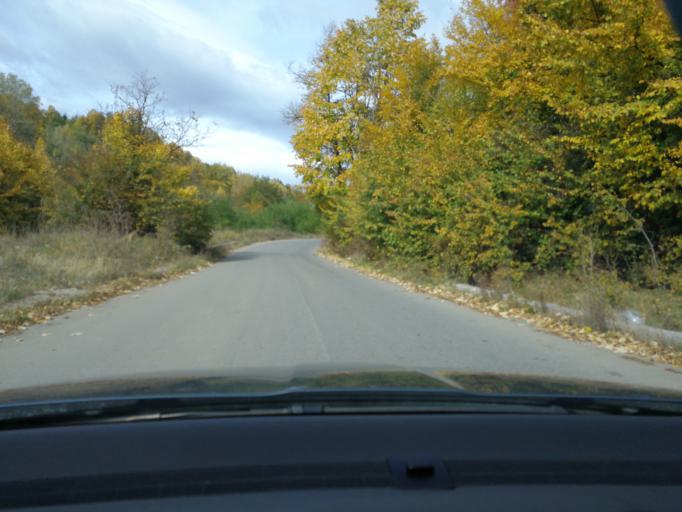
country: RO
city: Brebu Manastirei
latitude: 45.2032
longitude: 25.7854
